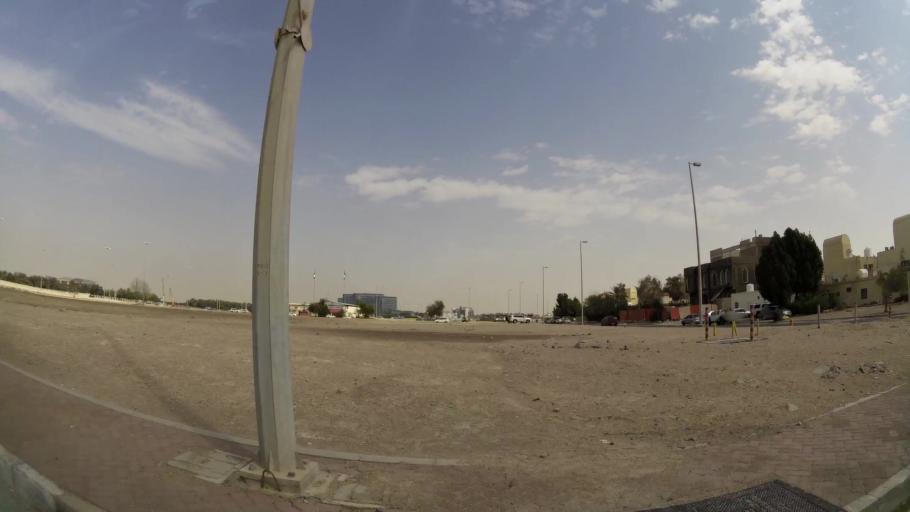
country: AE
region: Abu Dhabi
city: Abu Dhabi
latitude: 24.3125
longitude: 54.6064
